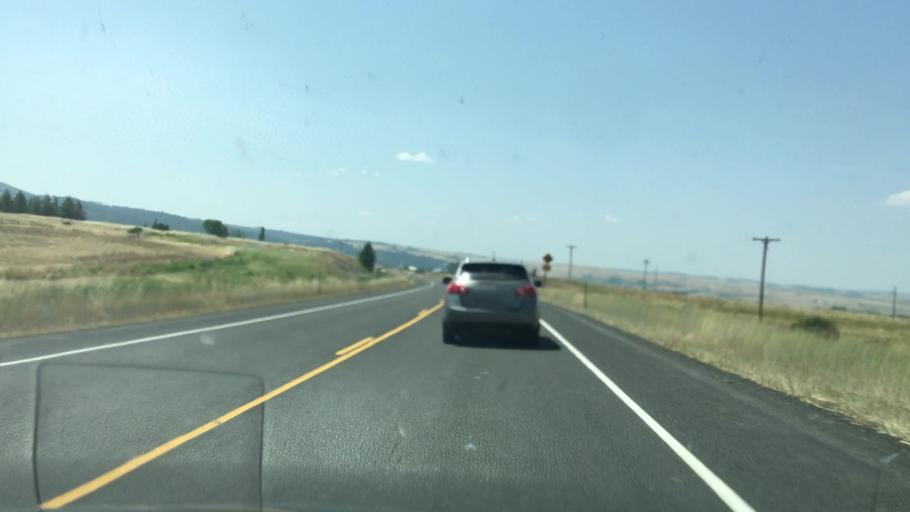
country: US
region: Idaho
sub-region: Idaho County
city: Grangeville
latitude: 45.9095
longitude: -116.1678
